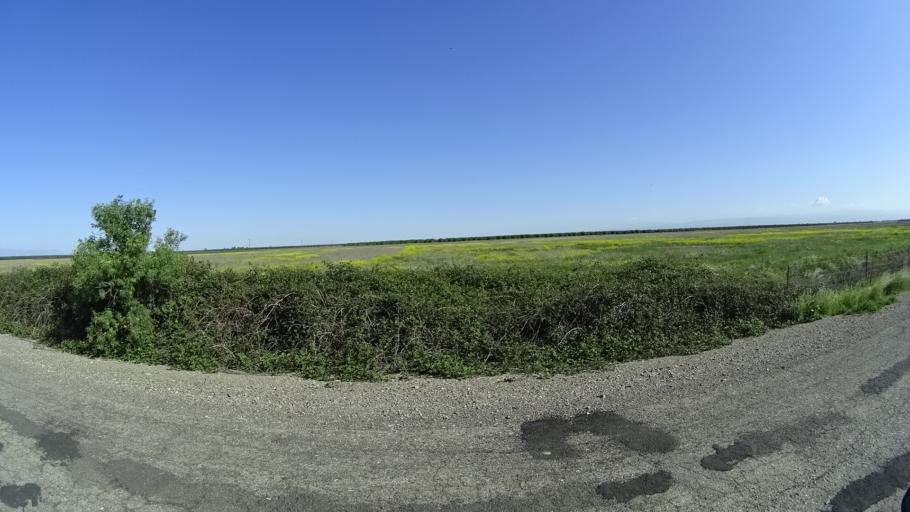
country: US
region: California
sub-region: Glenn County
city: Hamilton City
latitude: 39.6781
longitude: -122.0413
